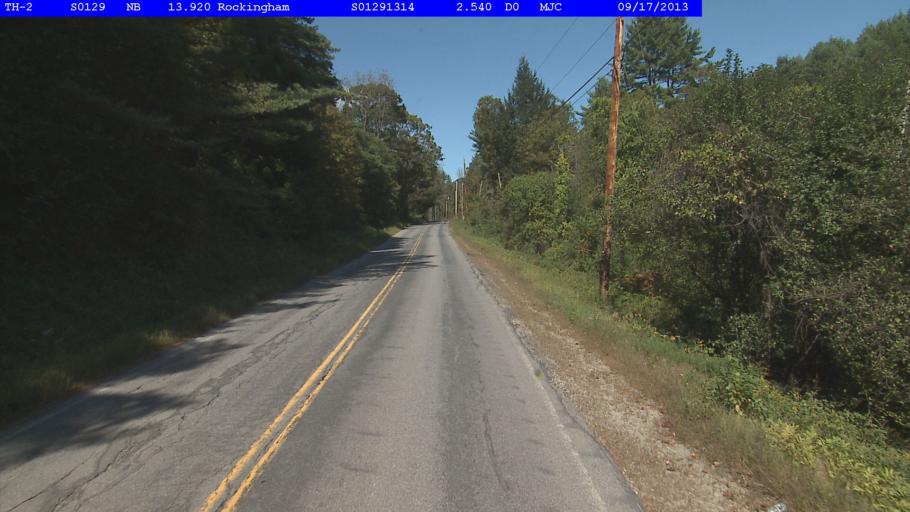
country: US
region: Vermont
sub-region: Windham County
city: Rockingham
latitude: 43.1540
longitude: -72.5175
